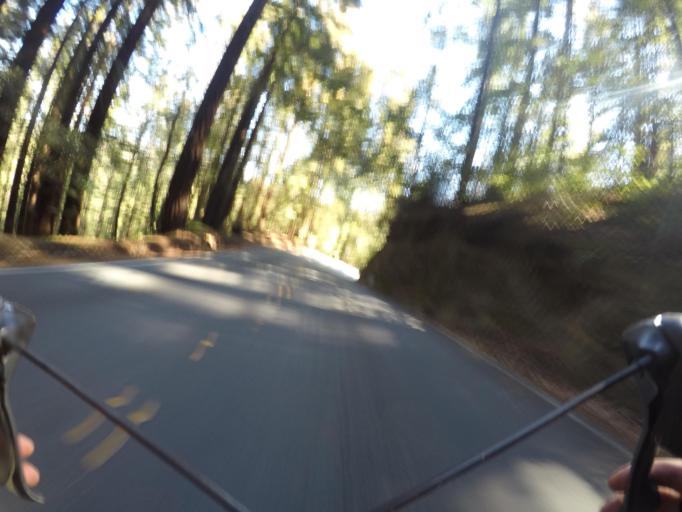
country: US
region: California
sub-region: San Mateo County
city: Portola Valley
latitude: 37.2996
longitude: -122.2704
